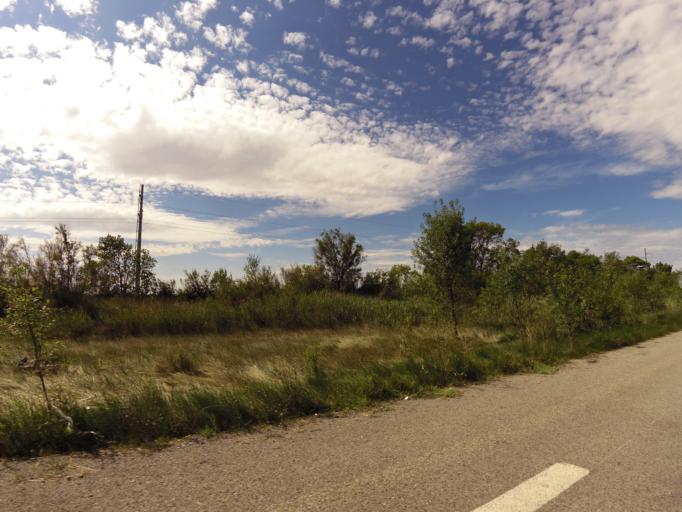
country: FR
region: Languedoc-Roussillon
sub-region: Departement du Gard
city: Aigues-Mortes
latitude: 43.5986
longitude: 4.1951
